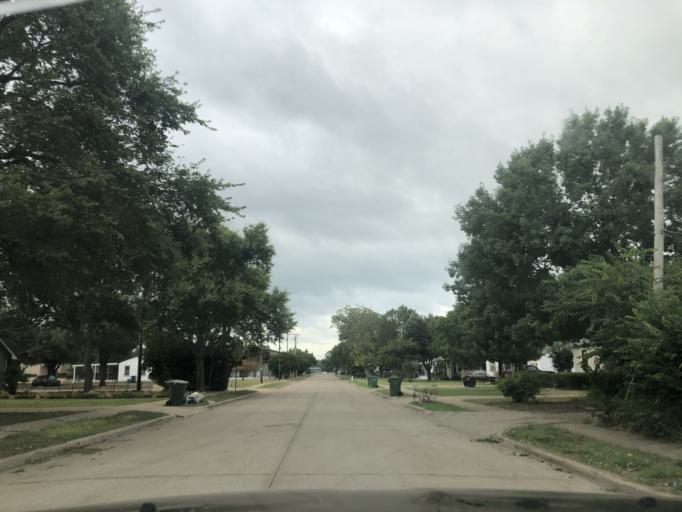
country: US
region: Texas
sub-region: Dallas County
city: Garland
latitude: 32.8825
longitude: -96.6493
